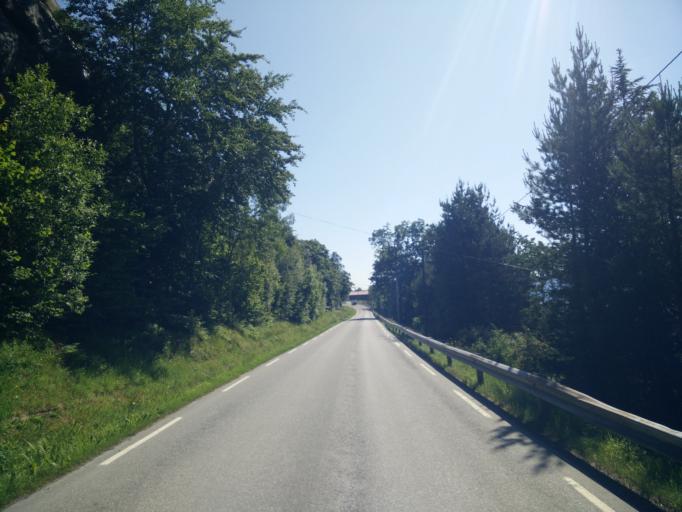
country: NO
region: More og Romsdal
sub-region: Kristiansund
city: Rensvik
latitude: 63.0272
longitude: 7.7919
